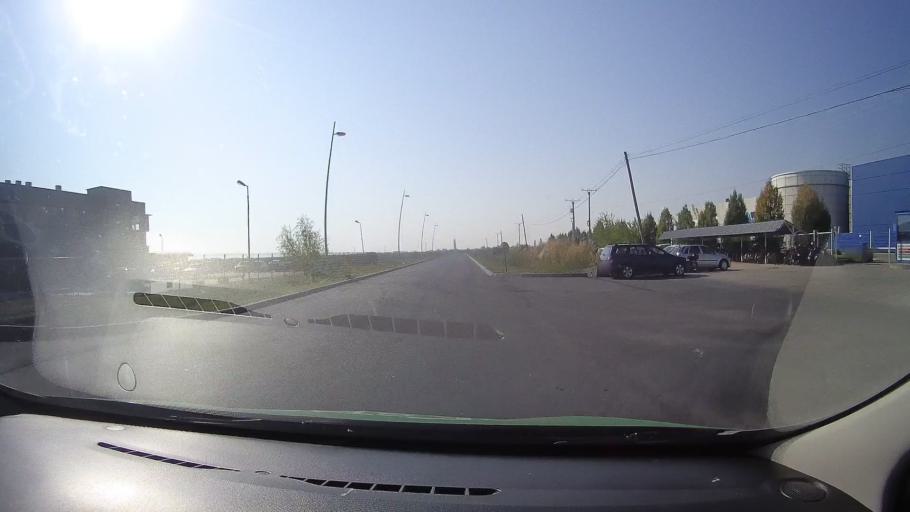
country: RO
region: Bihor
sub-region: Municipiul Salonta
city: Salonta
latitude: 46.7894
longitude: 21.6634
